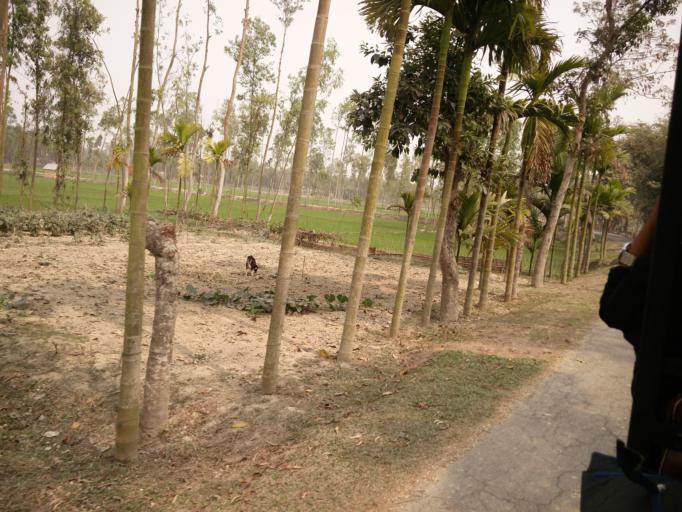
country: BD
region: Rangpur Division
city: Nageswari
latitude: 25.8821
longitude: 89.6951
